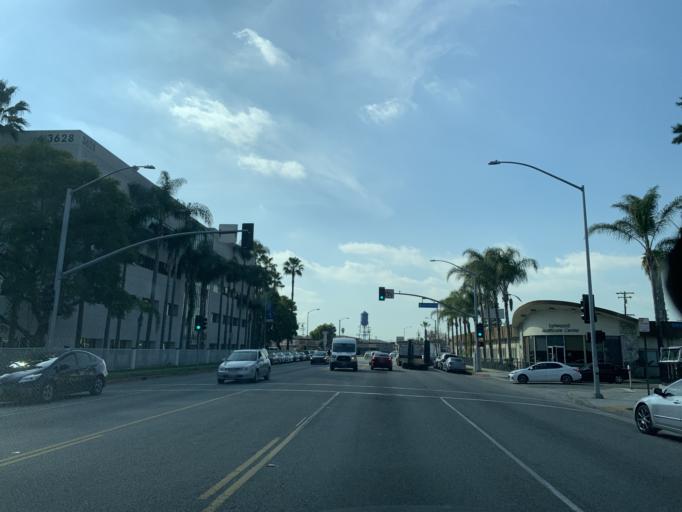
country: US
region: California
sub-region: Los Angeles County
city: Lynwood
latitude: 33.9311
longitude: -118.2039
